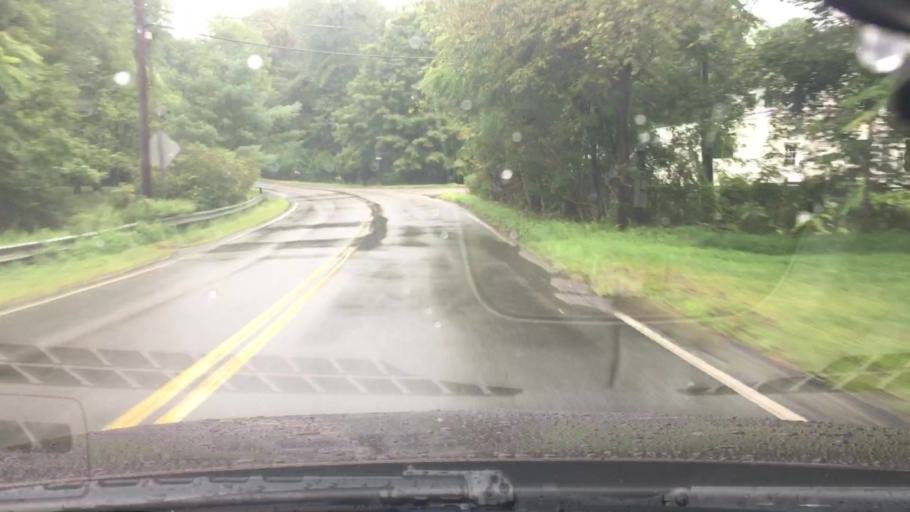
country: US
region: New York
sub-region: Dutchess County
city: Myers Corner
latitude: 41.5947
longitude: -73.8857
